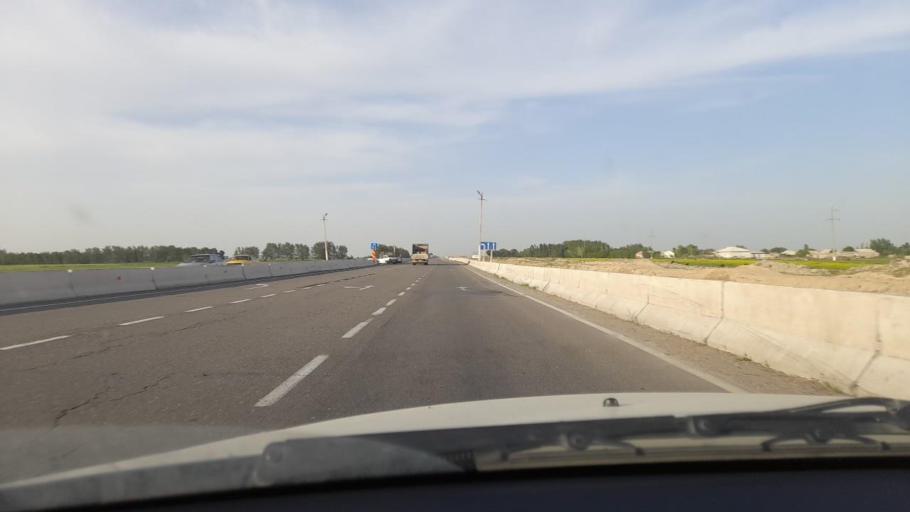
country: UZ
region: Jizzax
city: Paxtakor
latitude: 40.3219
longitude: 68.0973
